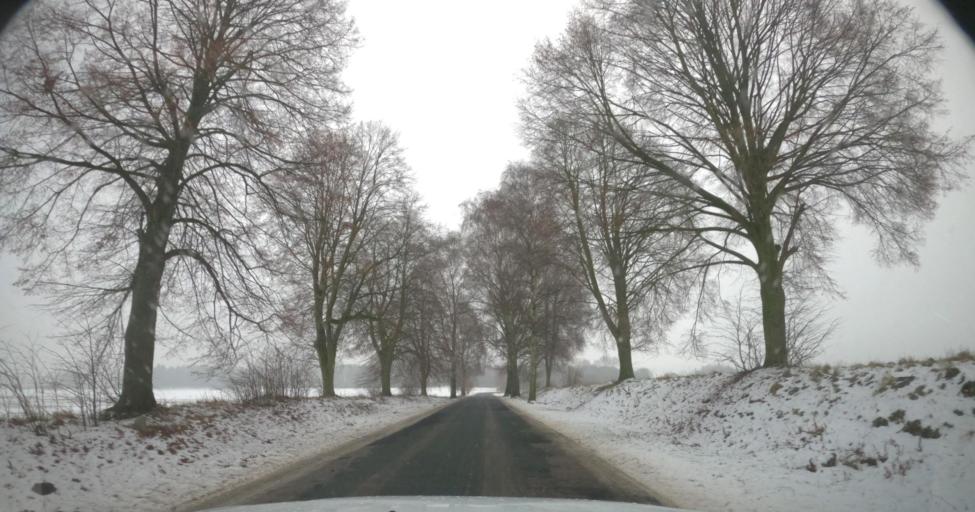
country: PL
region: West Pomeranian Voivodeship
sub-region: Powiat gryficki
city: Brojce
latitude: 53.9035
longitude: 15.2937
